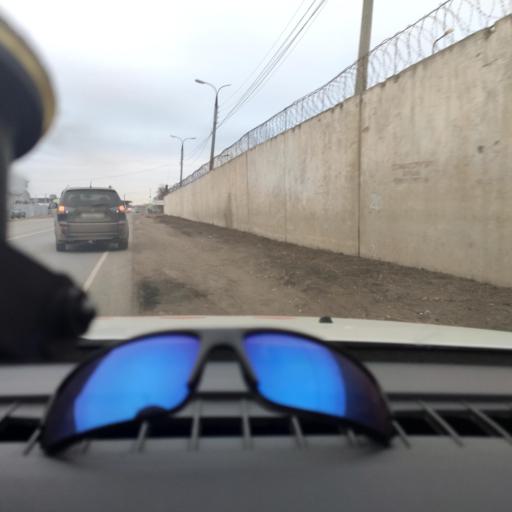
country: RU
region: Samara
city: Samara
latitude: 53.1342
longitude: 50.1056
